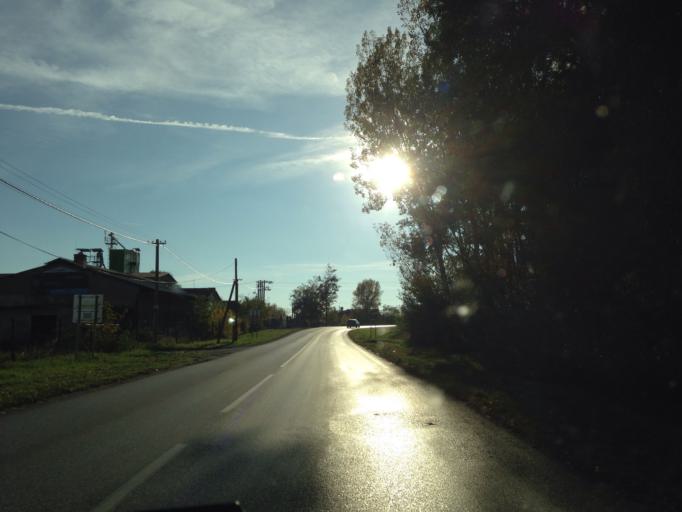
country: SK
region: Nitriansky
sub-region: Okres Komarno
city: Hurbanovo
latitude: 47.8120
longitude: 18.2173
